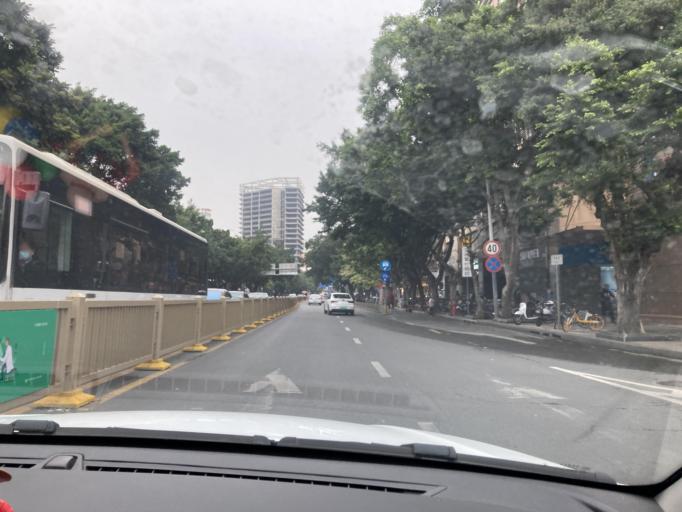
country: CN
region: Guangdong
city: Nantou
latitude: 22.5357
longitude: 113.9143
